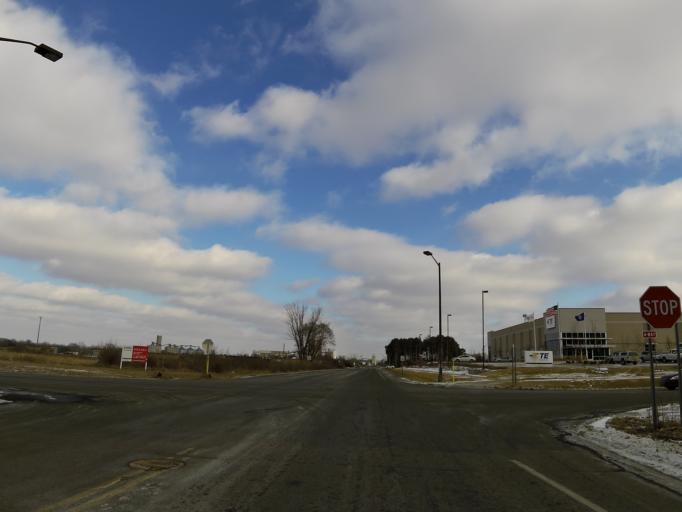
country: US
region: Minnesota
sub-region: Scott County
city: Shakopee
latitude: 44.7974
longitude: -93.4908
